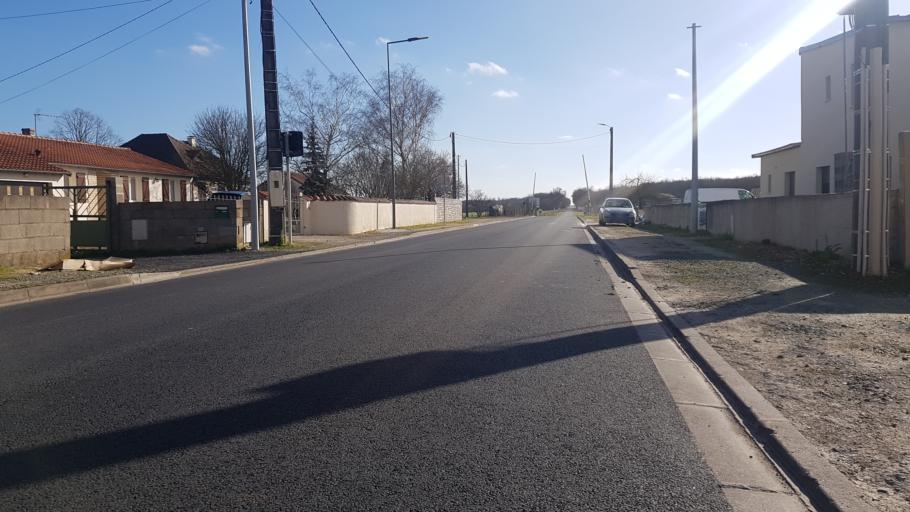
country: FR
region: Poitou-Charentes
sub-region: Departement de la Vienne
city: Avanton
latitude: 46.6578
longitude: 0.3048
